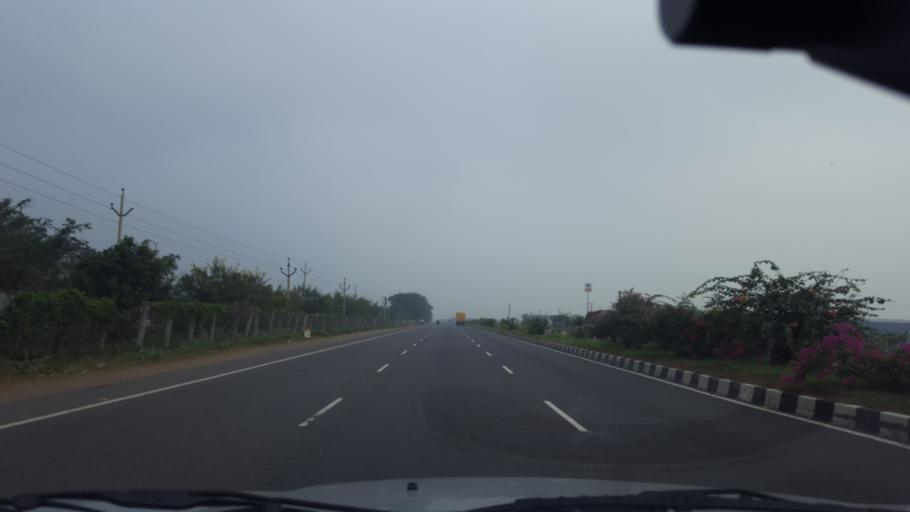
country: IN
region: Andhra Pradesh
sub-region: Prakasam
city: Addanki
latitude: 15.6684
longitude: 80.0155
